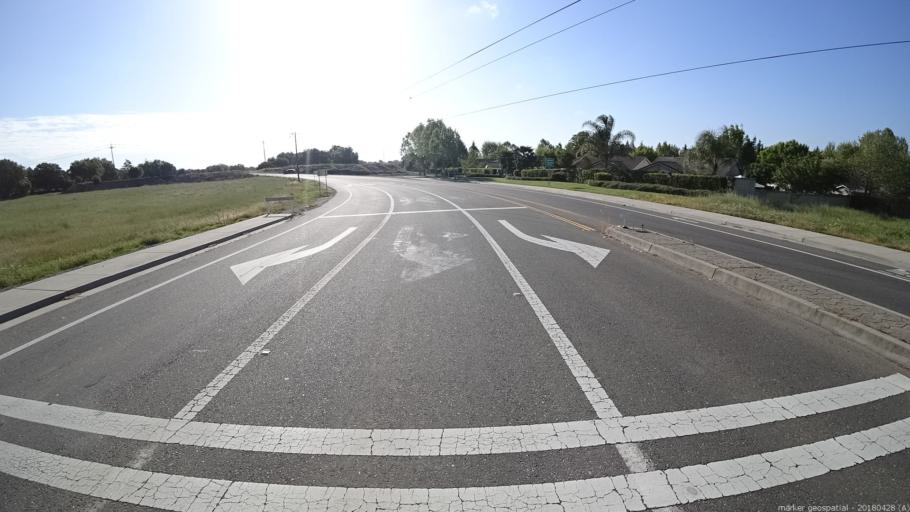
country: US
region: California
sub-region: Yolo County
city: West Sacramento
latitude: 38.5597
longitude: -121.5293
